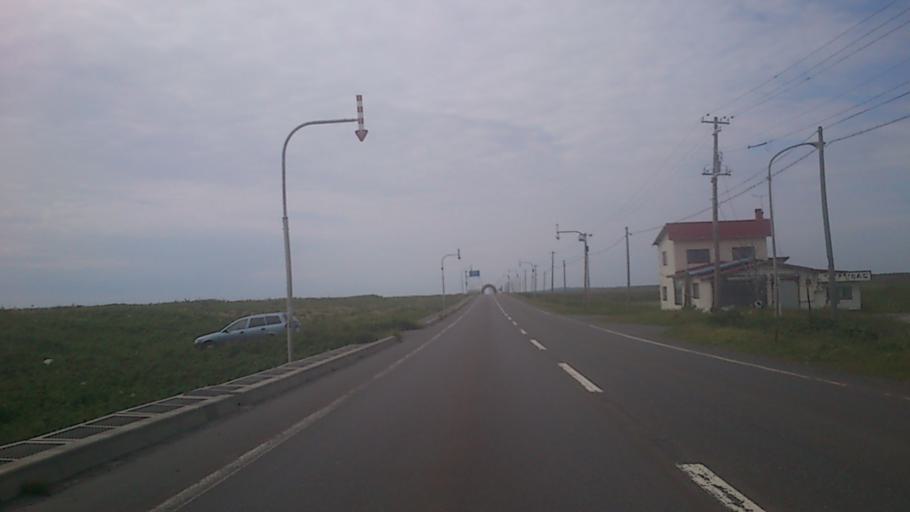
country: JP
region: Hokkaido
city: Makubetsu
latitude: 44.9973
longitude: 141.6840
